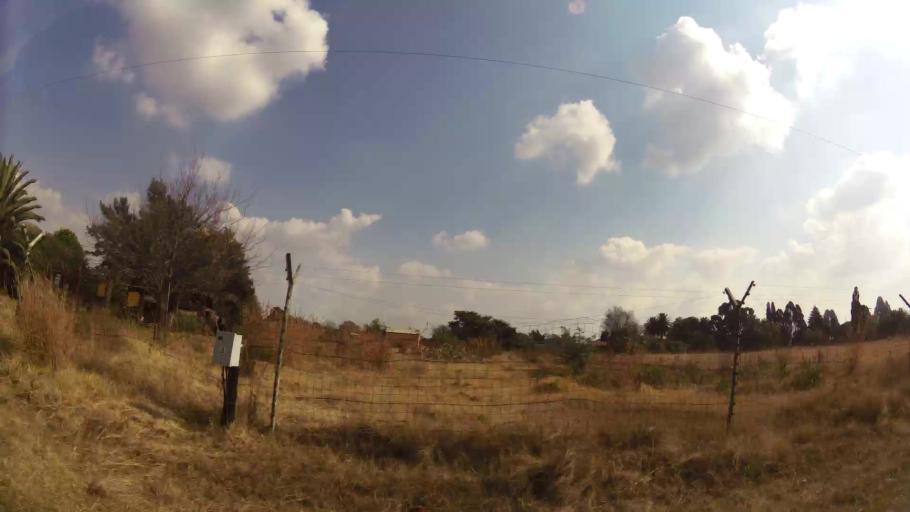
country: ZA
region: Mpumalanga
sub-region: Nkangala District Municipality
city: Delmas
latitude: -26.1743
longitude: 28.5408
